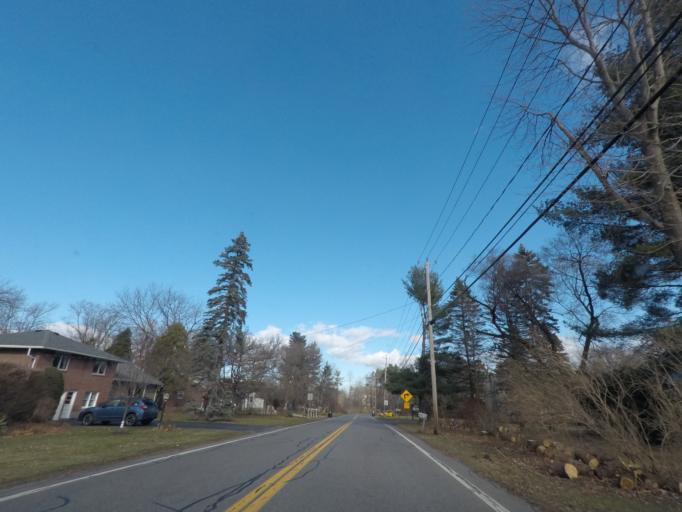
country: US
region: New York
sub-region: Schenectady County
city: Niskayuna
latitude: 42.8169
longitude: -73.8836
